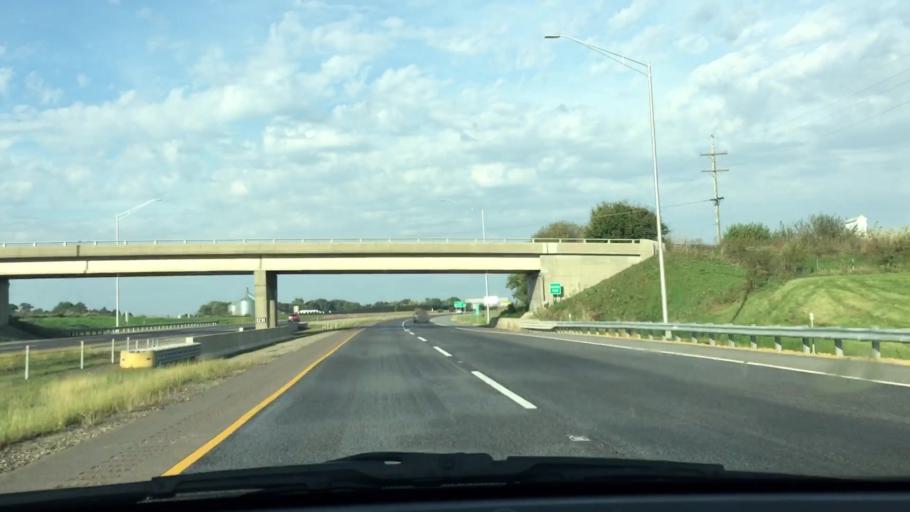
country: US
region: Illinois
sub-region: Lee County
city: Dixon
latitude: 41.8231
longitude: -89.4335
